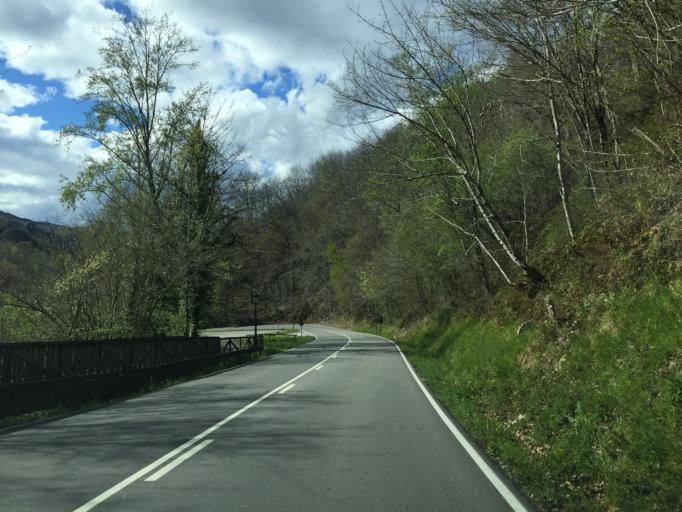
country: ES
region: Asturias
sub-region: Province of Asturias
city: Amieva
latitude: 43.3107
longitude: -5.0532
